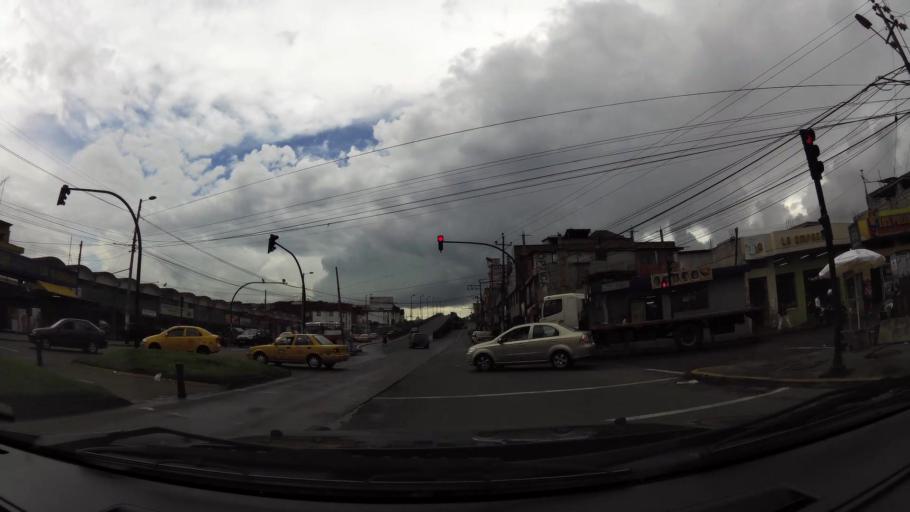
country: EC
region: Pichincha
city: Quito
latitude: -0.2763
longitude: -78.5524
